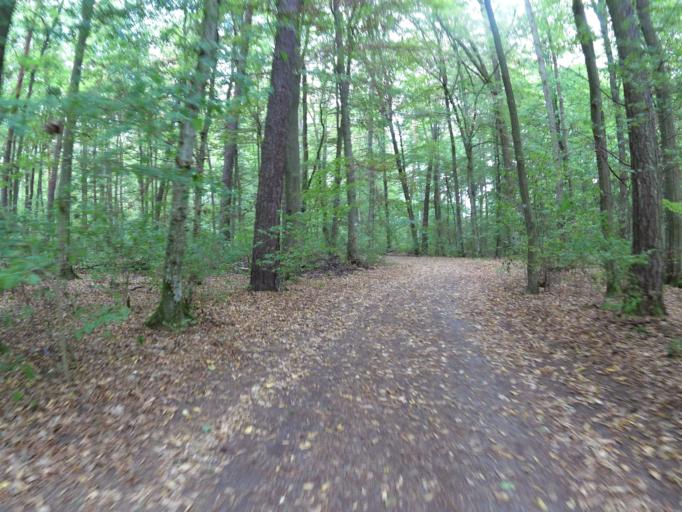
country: DE
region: Bavaria
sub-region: Regierungsbezirk Unterfranken
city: Waldbrunn
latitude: 49.7721
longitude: 9.8072
